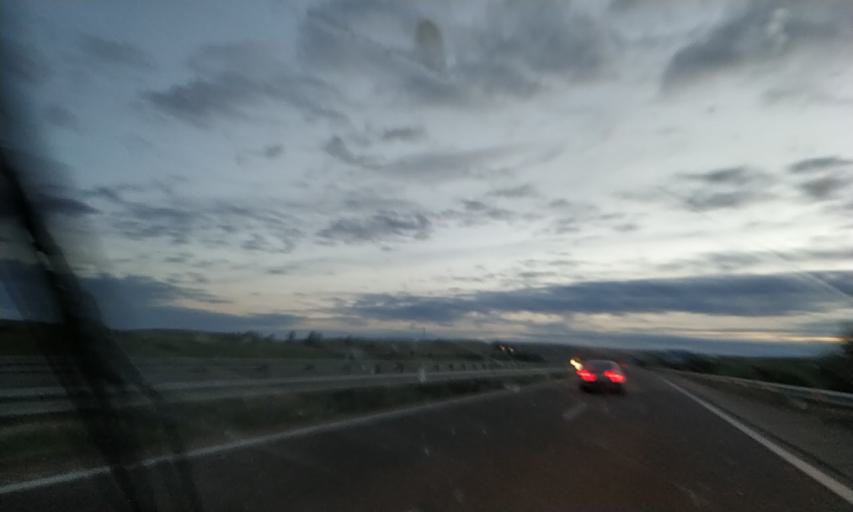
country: ES
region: Extremadura
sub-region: Provincia de Badajoz
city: Badajoz
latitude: 38.9175
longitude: -6.9787
